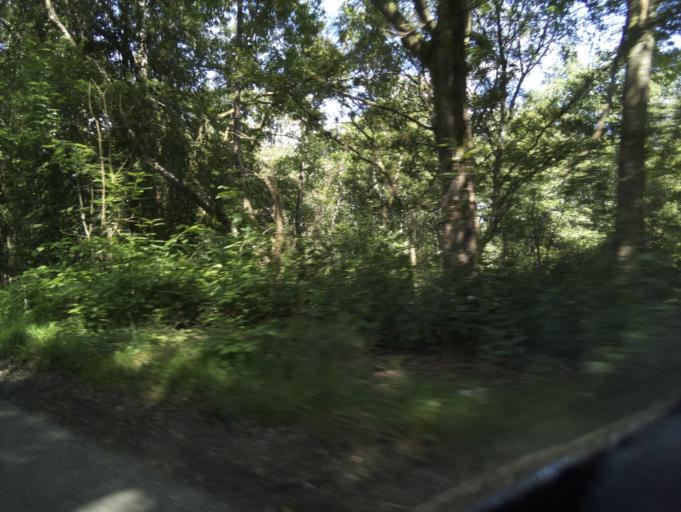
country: GB
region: England
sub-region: West Berkshire
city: Thatcham
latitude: 51.3758
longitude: -1.2464
